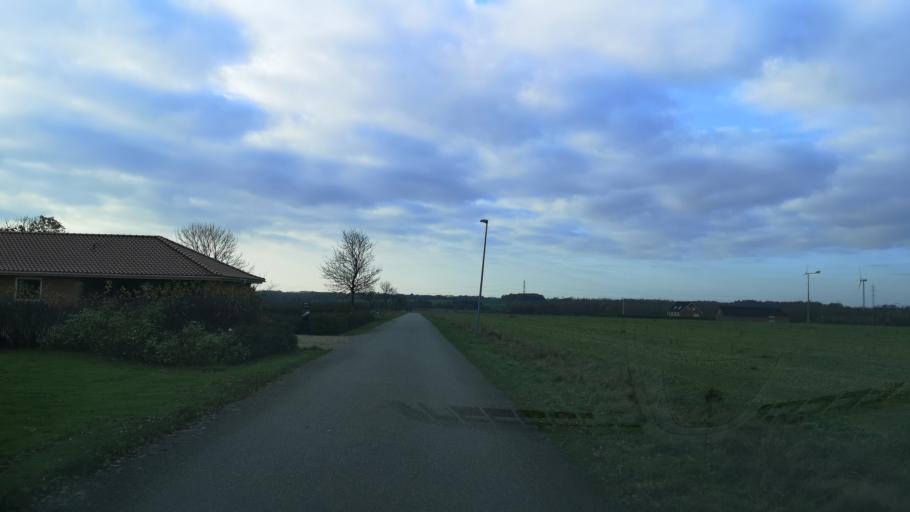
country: DK
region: Central Jutland
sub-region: Ringkobing-Skjern Kommune
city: Videbaek
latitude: 56.0074
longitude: 8.5984
